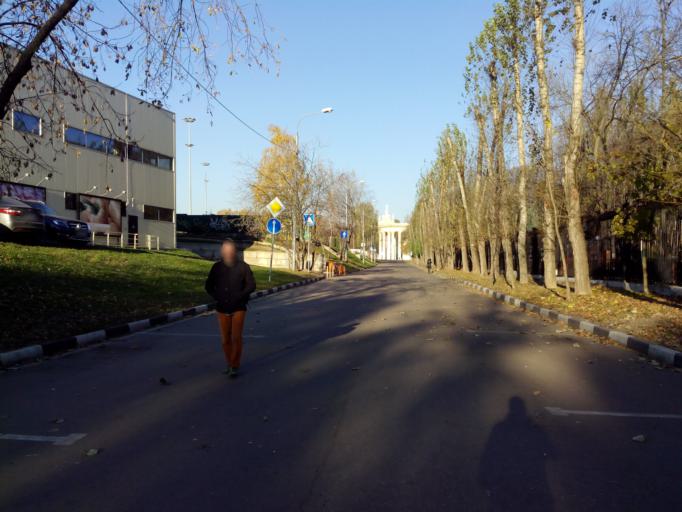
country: RU
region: Moscow
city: Ostankinskiy
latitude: 55.8251
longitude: 37.6351
